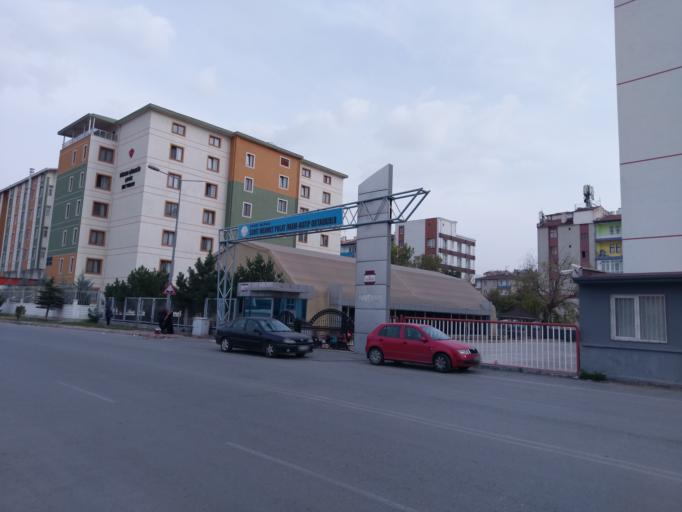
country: TR
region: Kayseri
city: Kayseri
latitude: 38.7117
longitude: 35.4886
